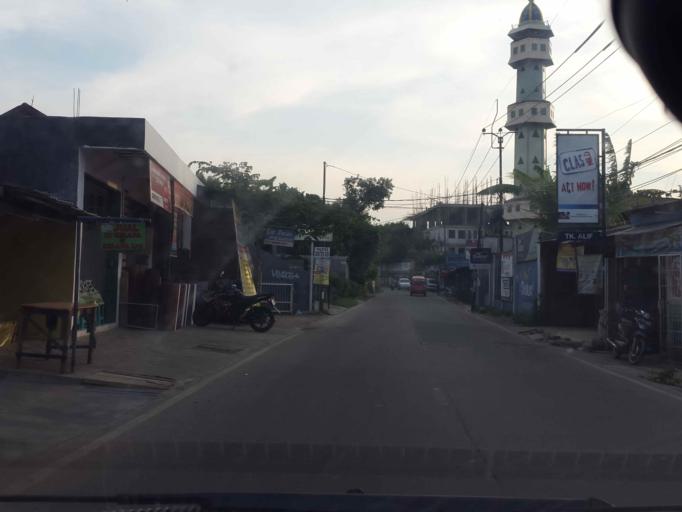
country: ID
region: Banten
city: South Tangerang
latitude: -6.2688
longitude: 106.7429
